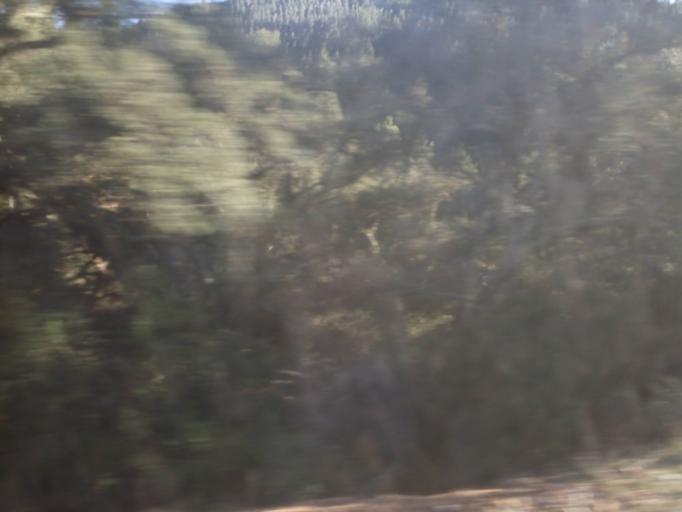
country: PT
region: Beja
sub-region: Odemira
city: Odemira
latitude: 37.6518
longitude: -8.4807
